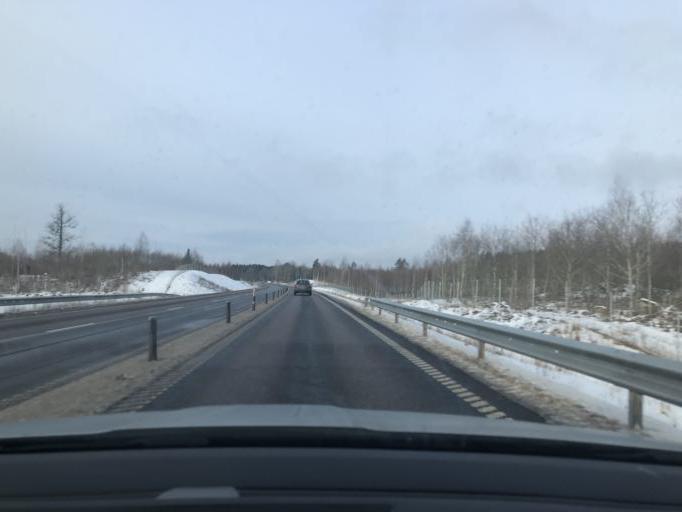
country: SE
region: OEstergoetland
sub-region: Motala Kommun
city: Borensberg
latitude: 58.5887
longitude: 15.1844
